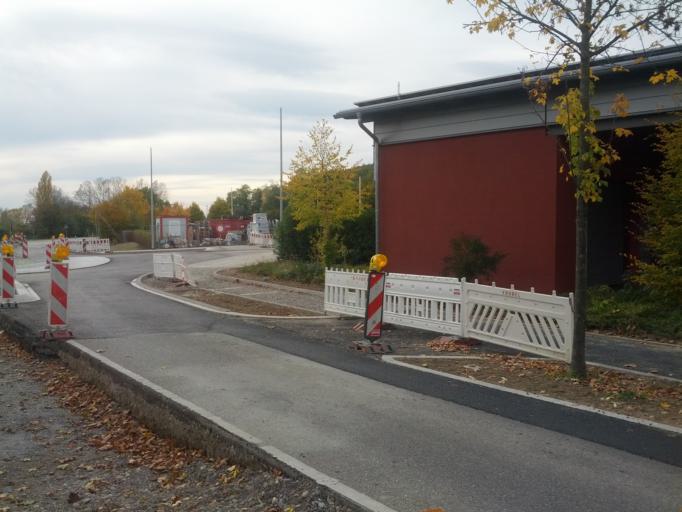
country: DE
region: Baden-Wuerttemberg
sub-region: Freiburg Region
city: Unterkrozingen
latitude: 47.9665
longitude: 7.6947
